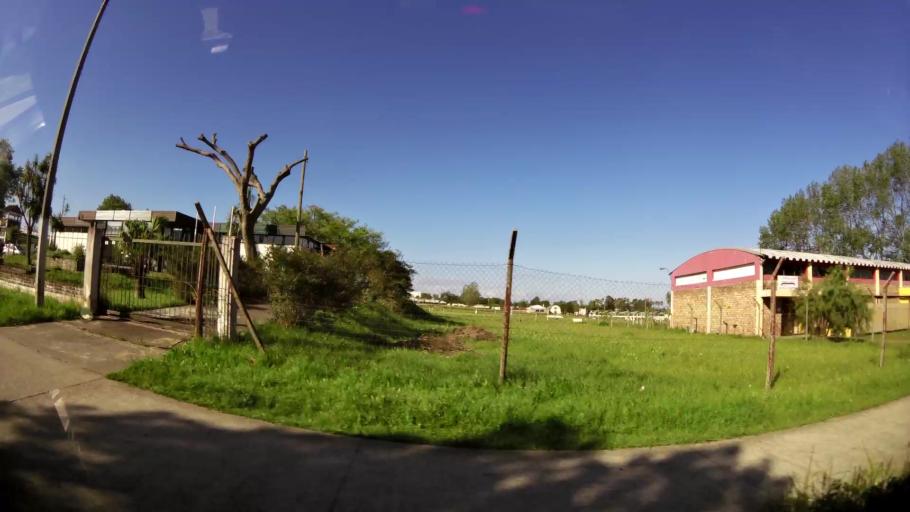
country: UY
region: Montevideo
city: Montevideo
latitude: -34.8308
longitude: -56.1895
